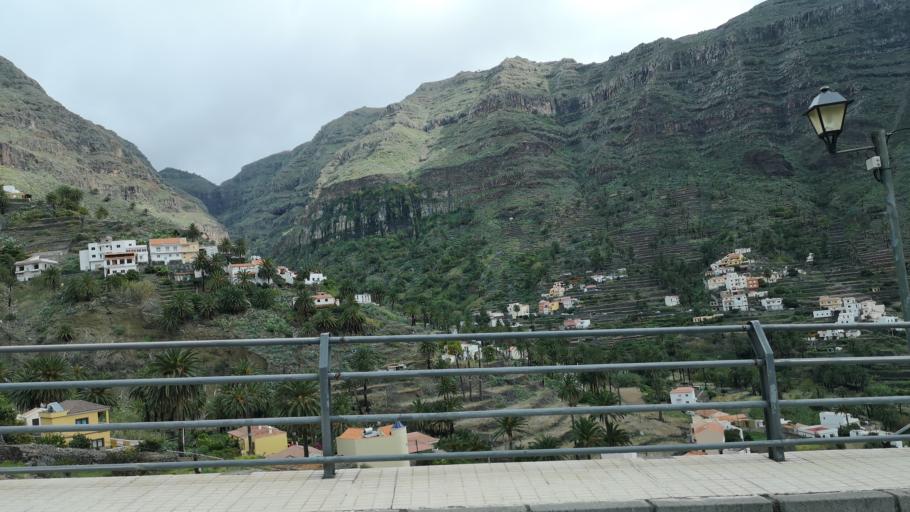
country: ES
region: Canary Islands
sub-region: Provincia de Santa Cruz de Tenerife
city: Vallehermosa
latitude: 28.1179
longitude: -17.3118
